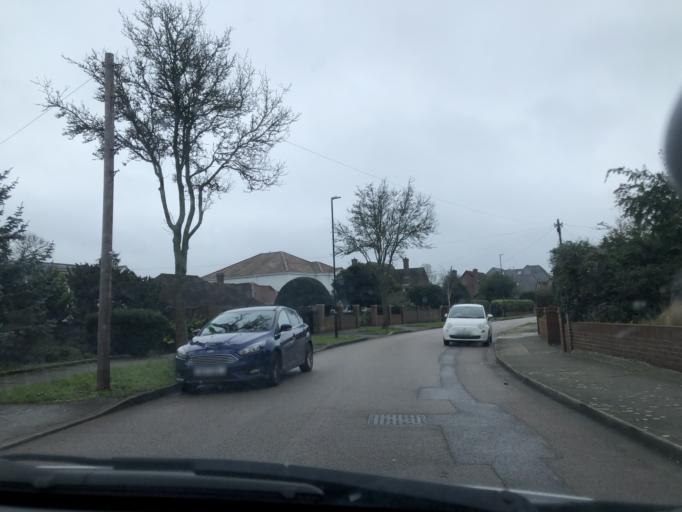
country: GB
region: England
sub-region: Greater London
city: Bexley
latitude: 51.4385
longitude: 0.1636
